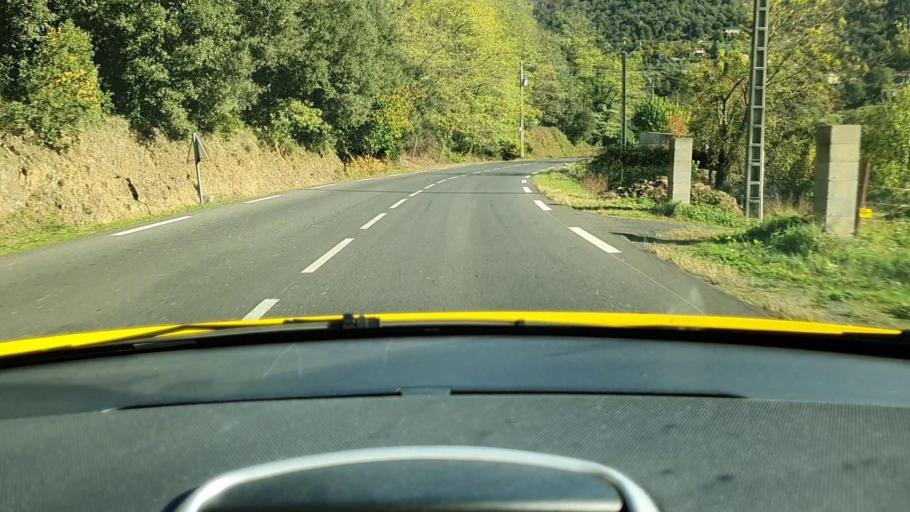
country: FR
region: Languedoc-Roussillon
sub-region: Departement du Gard
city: Sumene
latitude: 44.0230
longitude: 3.6815
